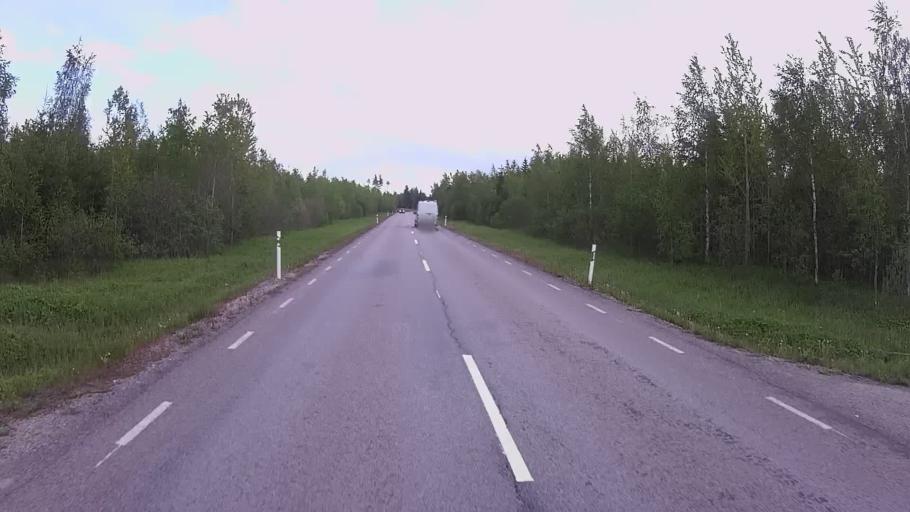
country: EE
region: Jogevamaa
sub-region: Mustvee linn
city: Mustvee
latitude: 59.0825
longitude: 26.9910
